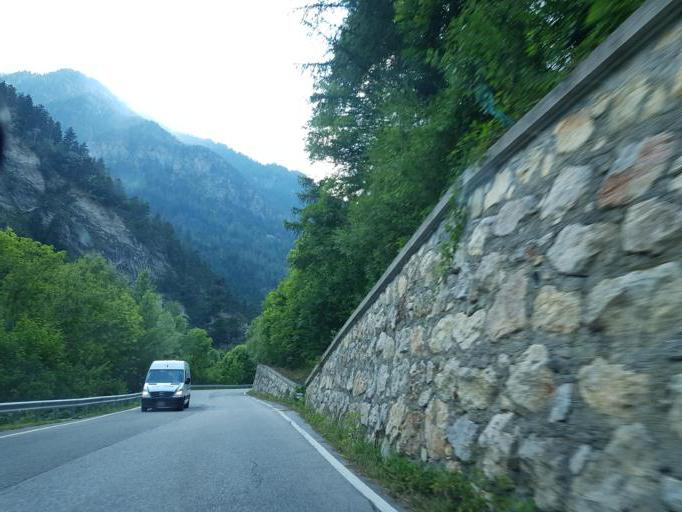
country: IT
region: Piedmont
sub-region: Provincia di Cuneo
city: Prazzo Superiore
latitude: 44.4783
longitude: 7.0473
